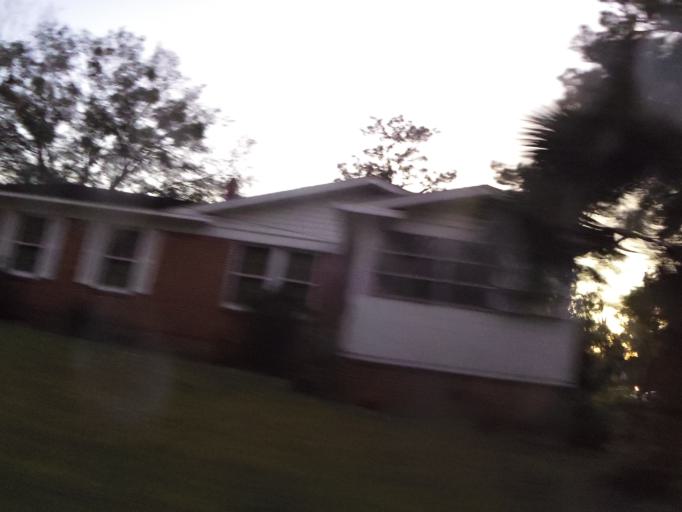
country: US
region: Florida
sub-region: Duval County
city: Jacksonville
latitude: 30.2995
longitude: -81.7077
